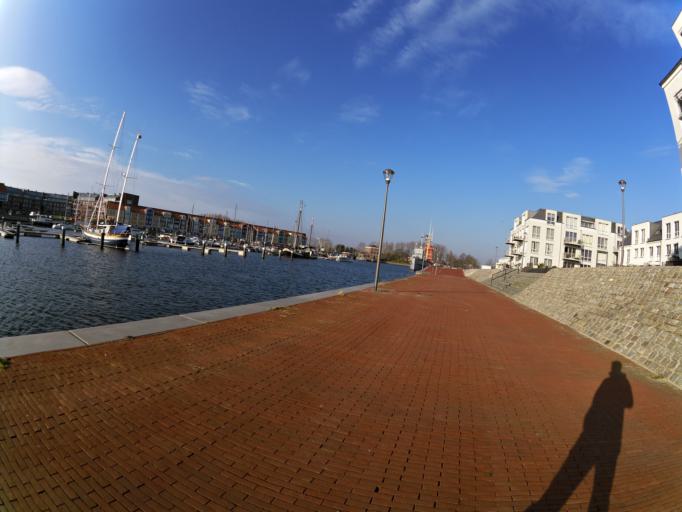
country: NL
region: South Holland
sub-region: Gemeente Hellevoetsluis
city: Hellevoetsluis
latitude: 51.8259
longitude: 4.1301
